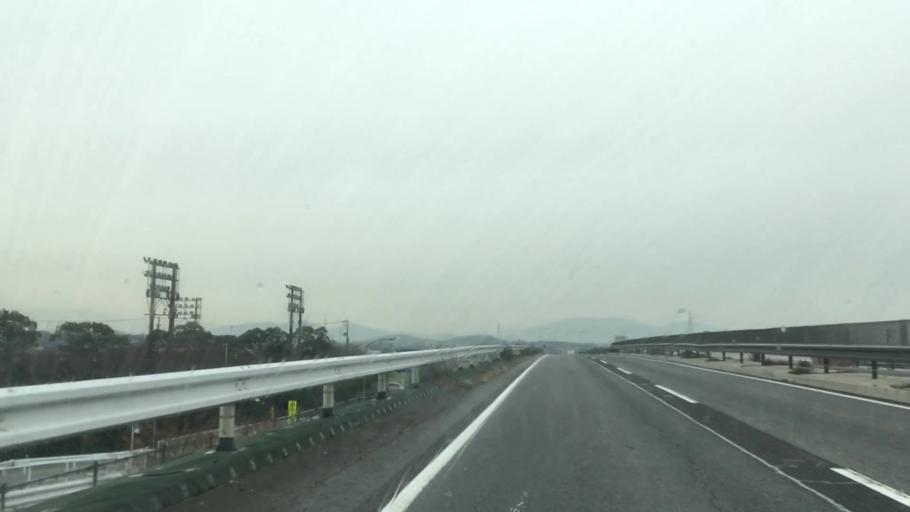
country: JP
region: Aichi
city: Nishio
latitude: 34.8999
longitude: 137.0702
